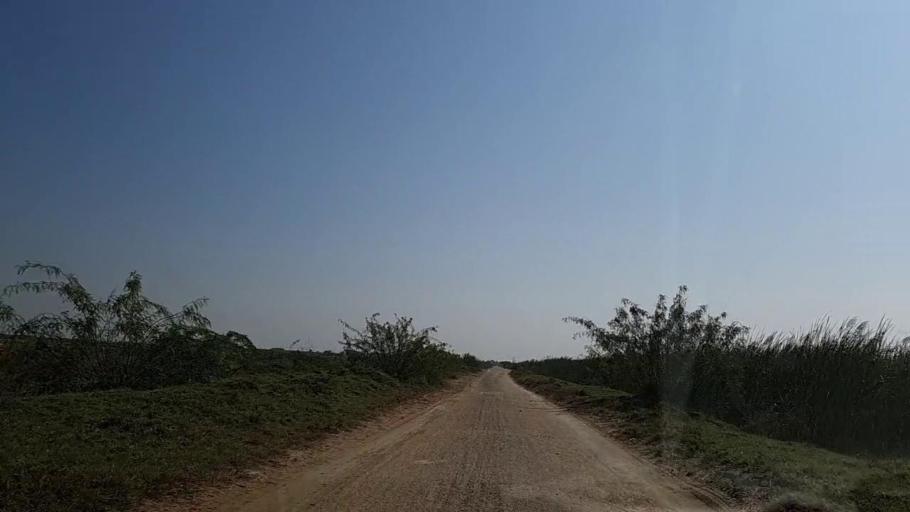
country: PK
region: Sindh
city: Chuhar Jamali
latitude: 24.4672
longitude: 68.0966
